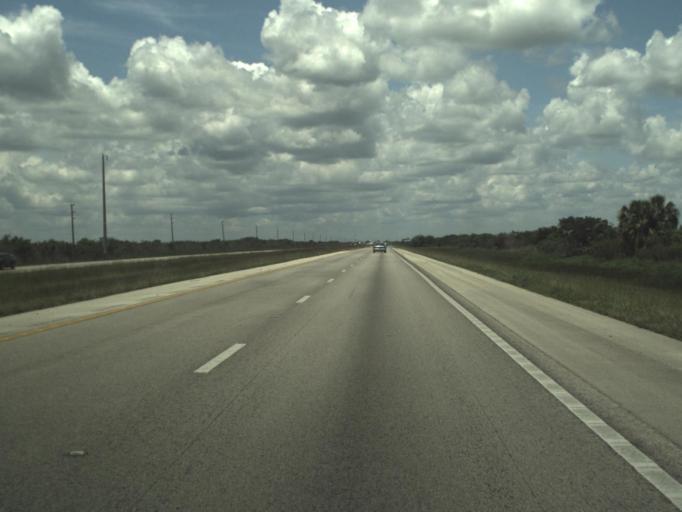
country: US
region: Florida
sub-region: Broward County
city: Weston
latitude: 26.1621
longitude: -80.7997
